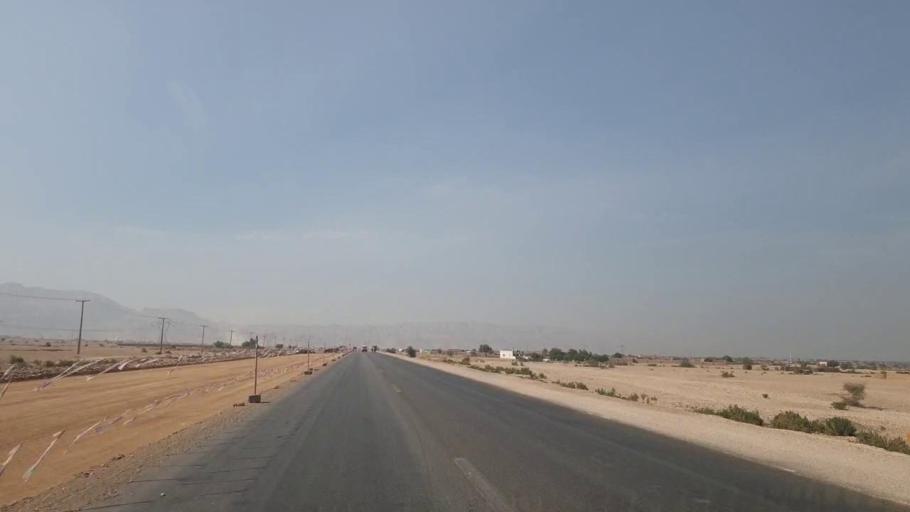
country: PK
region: Sindh
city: Sehwan
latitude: 26.1997
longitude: 67.9398
